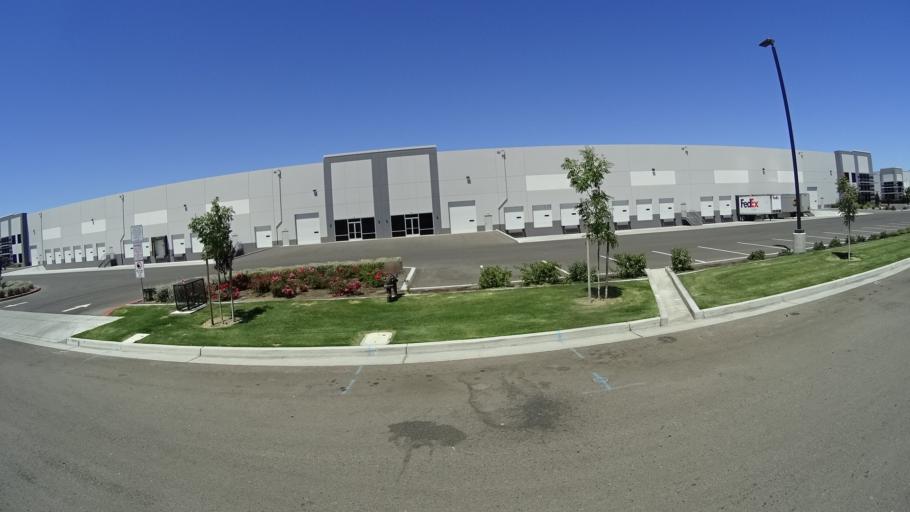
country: US
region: California
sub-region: Fresno County
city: Easton
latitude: 36.6857
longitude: -119.7675
